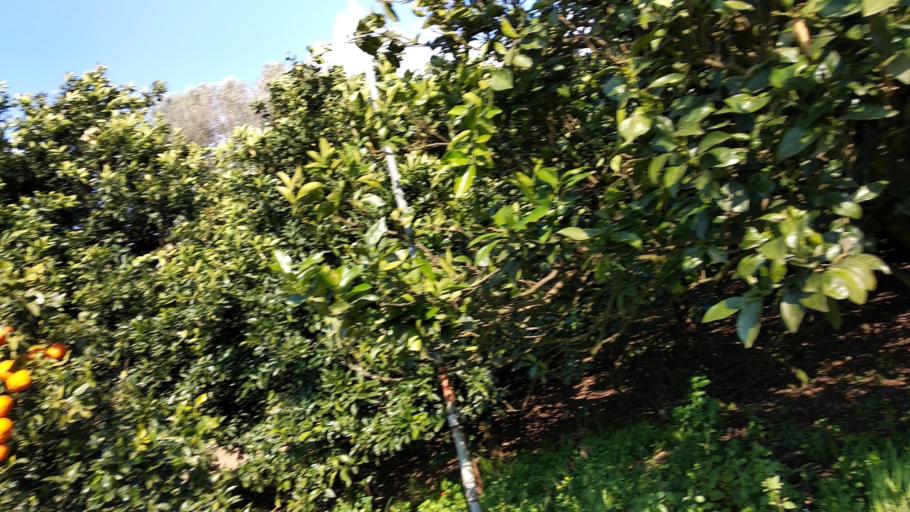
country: IT
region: Calabria
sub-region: Provincia di Reggio Calabria
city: Rizziconi
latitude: 38.4307
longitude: 15.9595
